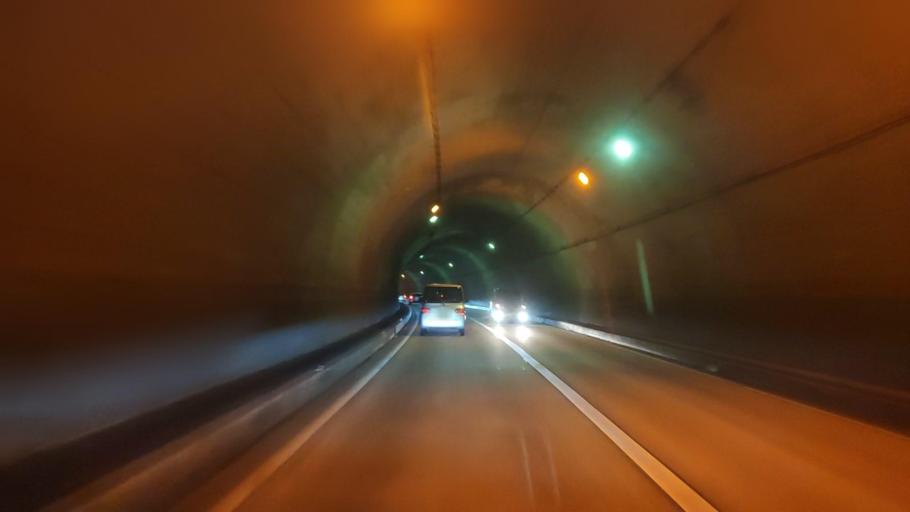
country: JP
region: Wakayama
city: Tanabe
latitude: 33.7300
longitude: 135.4350
